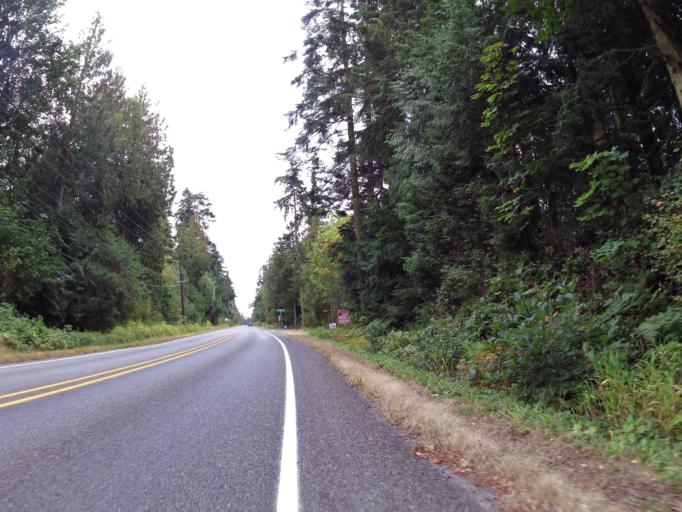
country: US
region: Washington
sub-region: Jefferson County
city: Port Ludlow
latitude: 47.9867
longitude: -122.7210
